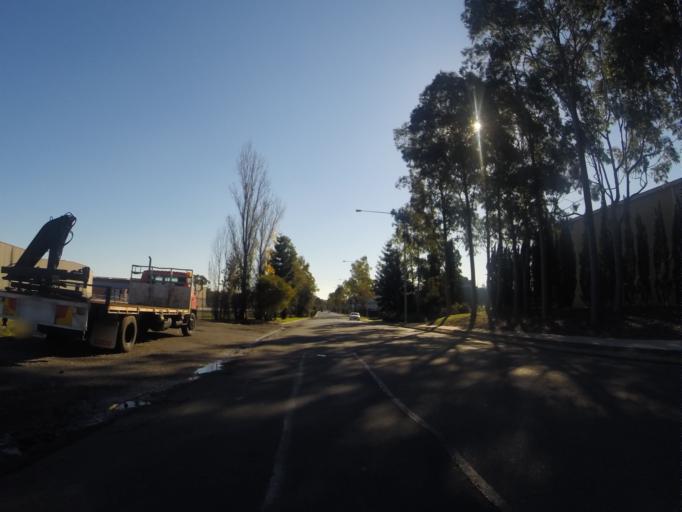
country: AU
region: New South Wales
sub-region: Bankstown
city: Regents Park
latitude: -33.8812
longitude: 151.0187
